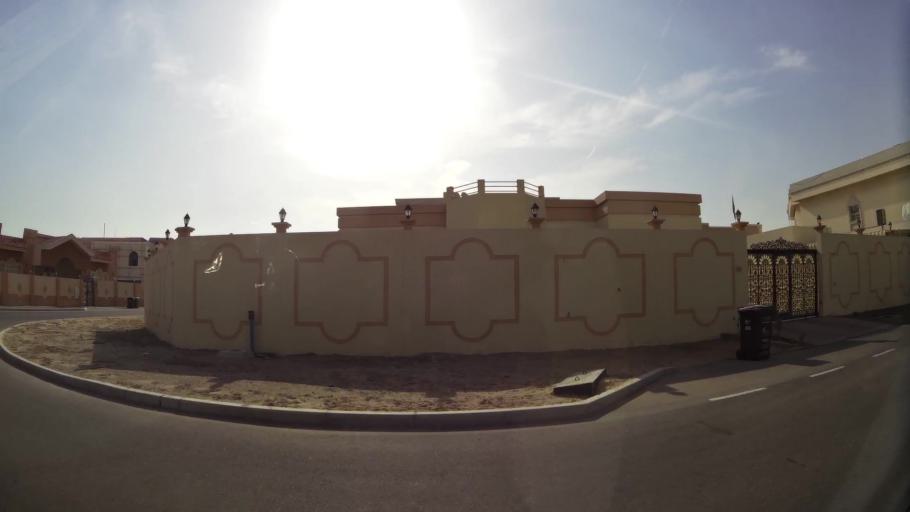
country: AE
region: Ash Shariqah
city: Sharjah
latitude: 25.2416
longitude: 55.4092
